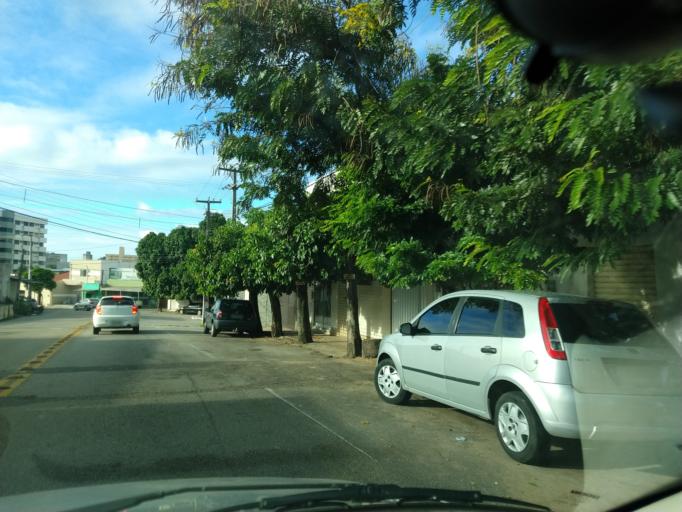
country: BR
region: Rio Grande do Norte
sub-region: Natal
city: Natal
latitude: -5.7952
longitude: -35.2092
